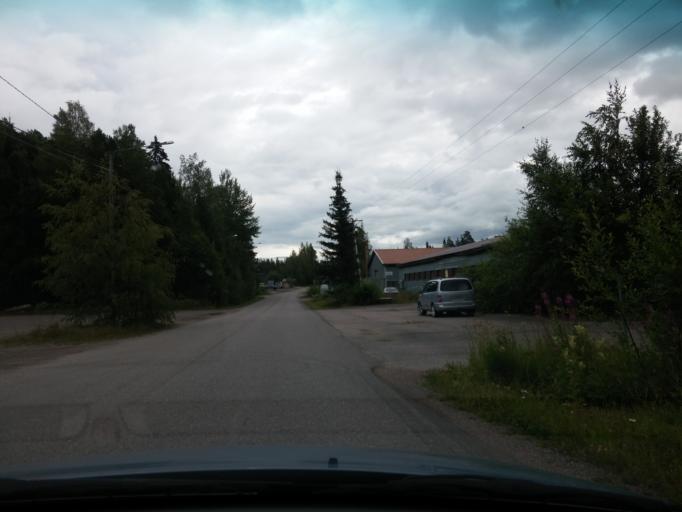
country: FI
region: Uusimaa
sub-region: Porvoo
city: Askola
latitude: 60.5024
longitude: 25.5635
